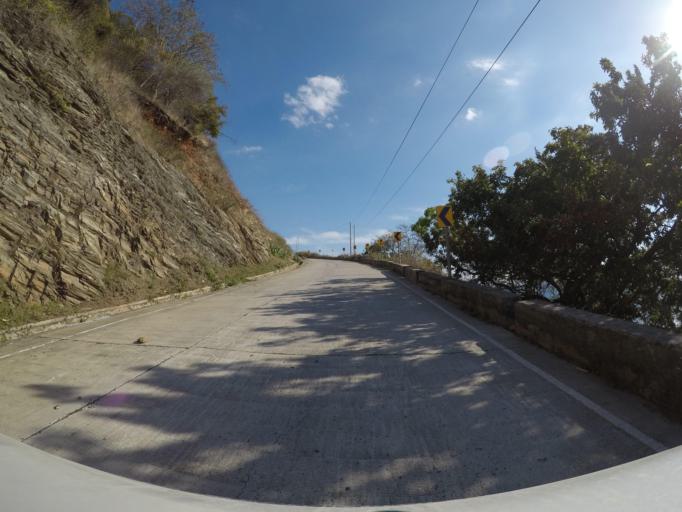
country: TL
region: Liquica
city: Maubara
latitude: -8.6699
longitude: 125.1088
